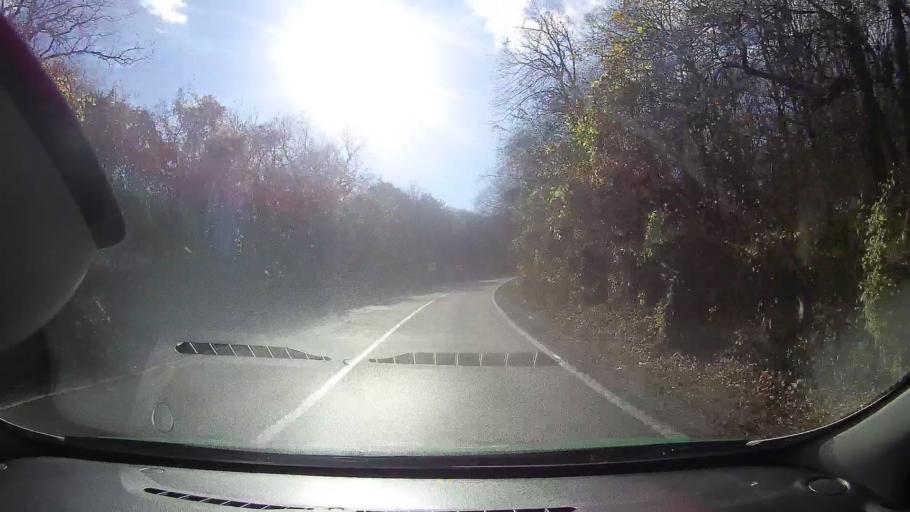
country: RO
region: Tulcea
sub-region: Oras Babadag
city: Babadag
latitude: 44.8428
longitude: 28.6976
